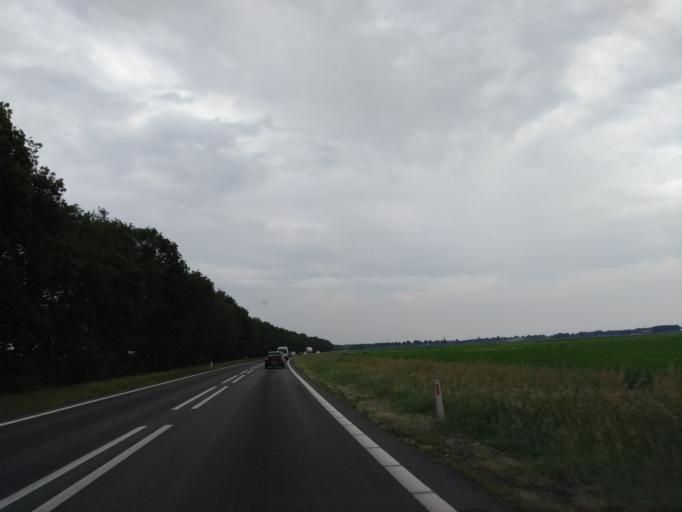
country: NL
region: Overijssel
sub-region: Gemeente Twenterand
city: Westerhaar-Vriezenveensewijk
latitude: 52.4856
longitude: 6.6052
